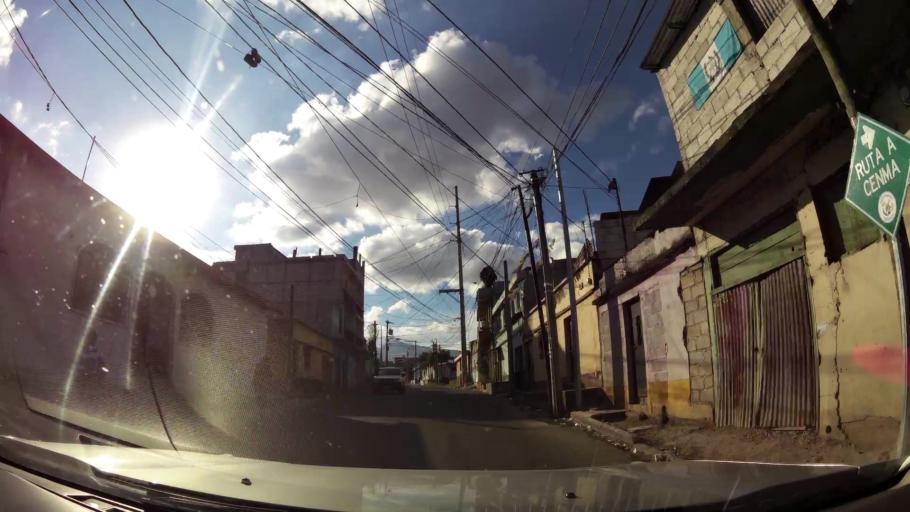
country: GT
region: Guatemala
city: Villa Nueva
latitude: 14.5261
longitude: -90.5794
